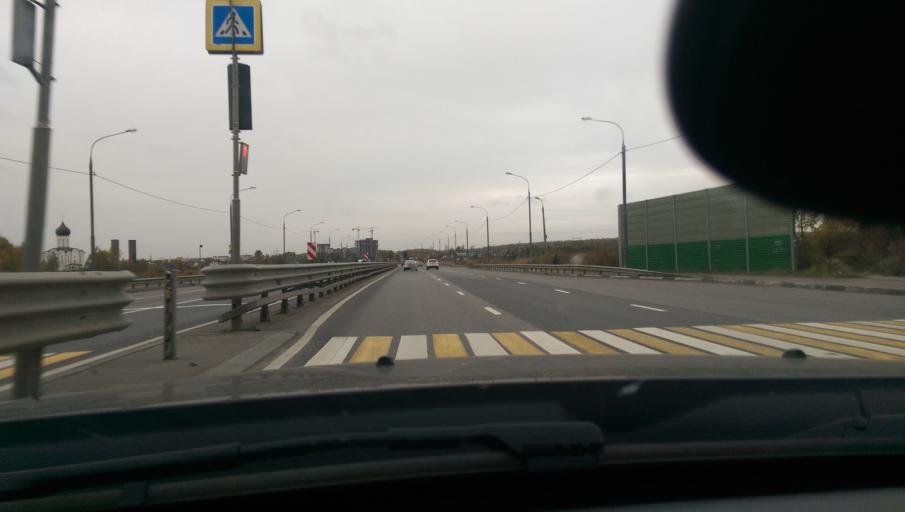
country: RU
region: Moscow
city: Vatutino
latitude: 55.9326
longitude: 37.6581
